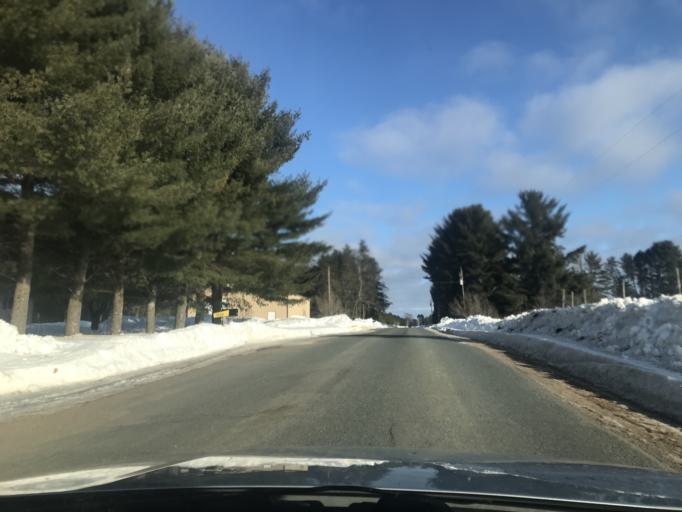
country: US
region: Wisconsin
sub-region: Marinette County
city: Niagara
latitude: 45.6099
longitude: -87.9769
